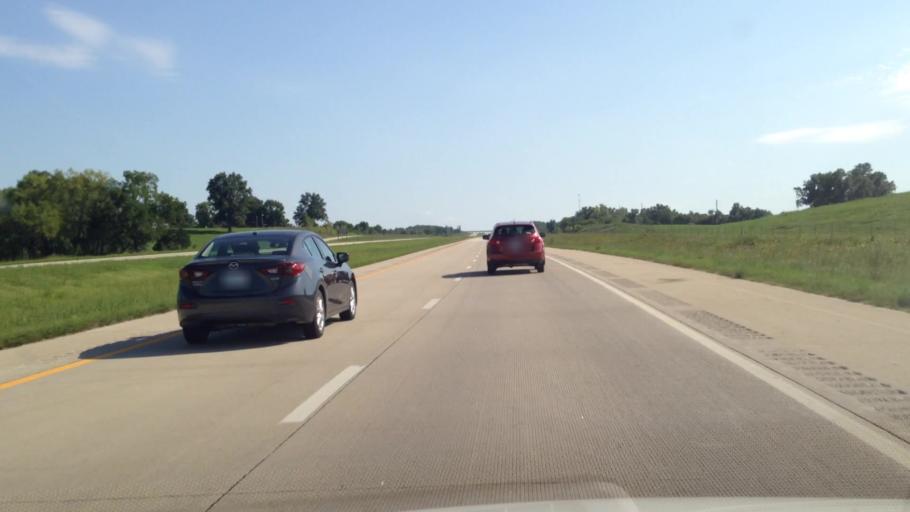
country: US
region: Kansas
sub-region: Linn County
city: Pleasanton
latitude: 38.1341
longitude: -94.7139
